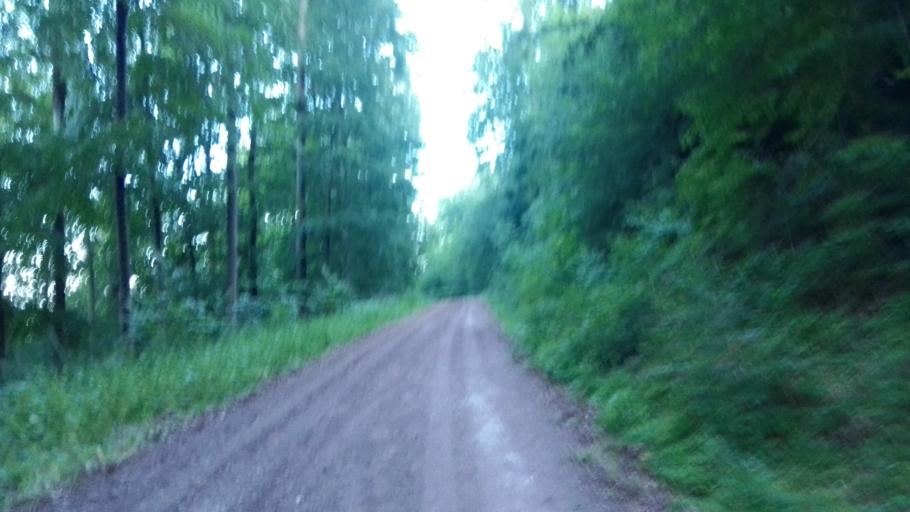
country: DE
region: Lower Saxony
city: Salzhemmendorf
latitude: 52.0305
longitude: 9.5848
